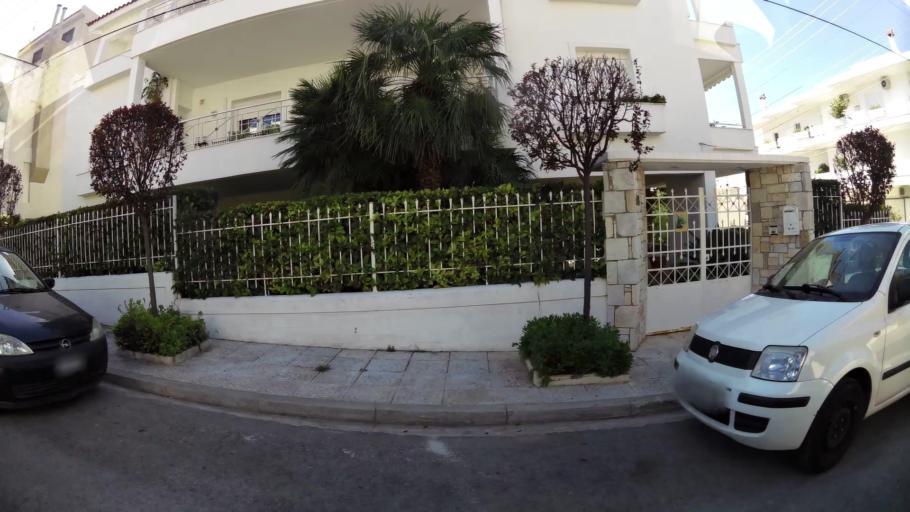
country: GR
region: Attica
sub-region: Nomarchia Anatolikis Attikis
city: Voula
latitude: 37.8445
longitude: 23.7733
